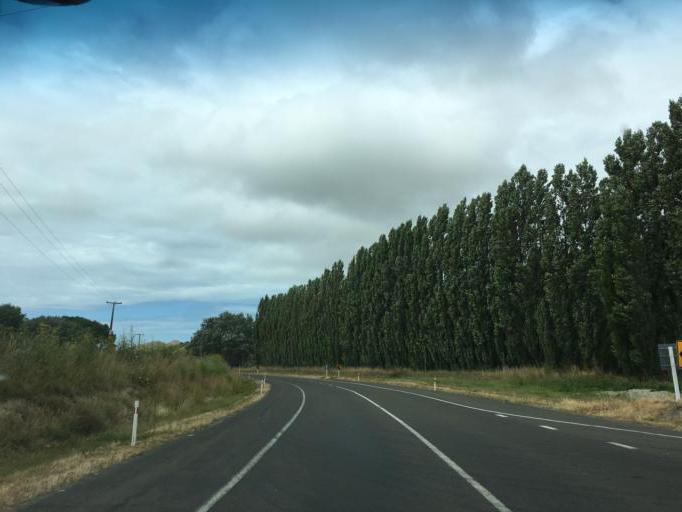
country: NZ
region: Gisborne
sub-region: Gisborne District
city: Gisborne
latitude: -38.5790
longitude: 178.1806
